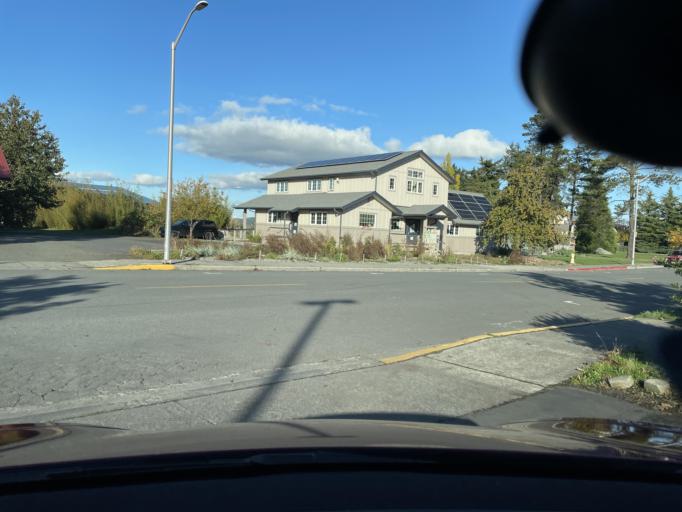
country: US
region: Washington
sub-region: San Juan County
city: Friday Harbor
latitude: 48.5300
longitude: -123.0205
